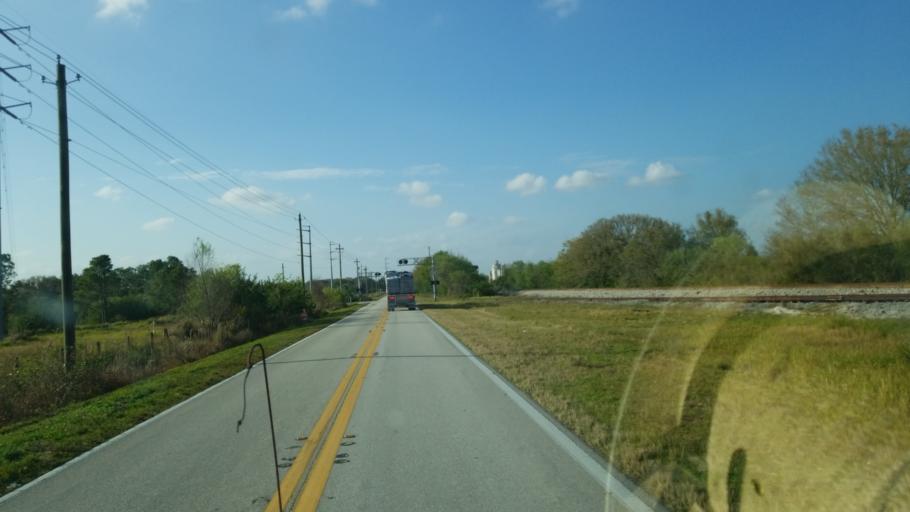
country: US
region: Florida
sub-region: Polk County
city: Mulberry
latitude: 27.7281
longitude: -81.9687
